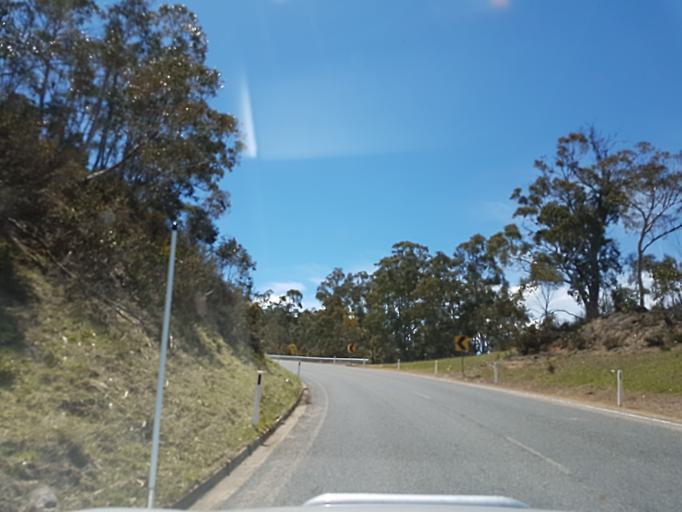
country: AU
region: Victoria
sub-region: Alpine
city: Mount Beauty
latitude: -37.0833
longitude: 147.3883
